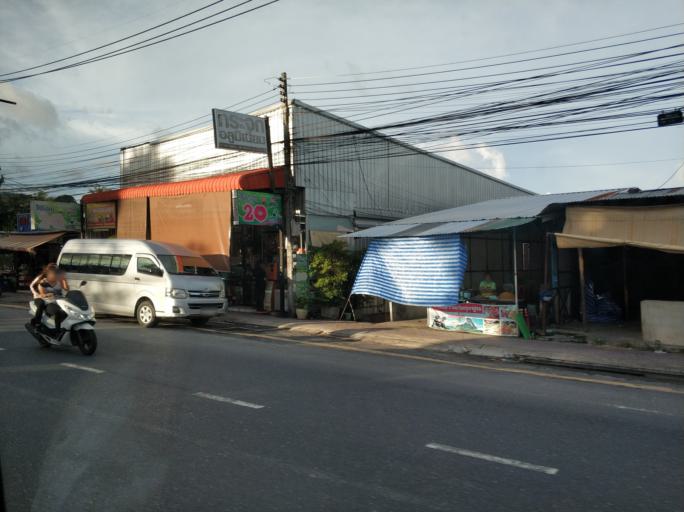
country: TH
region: Phuket
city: Kathu
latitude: 7.9087
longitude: 98.3352
